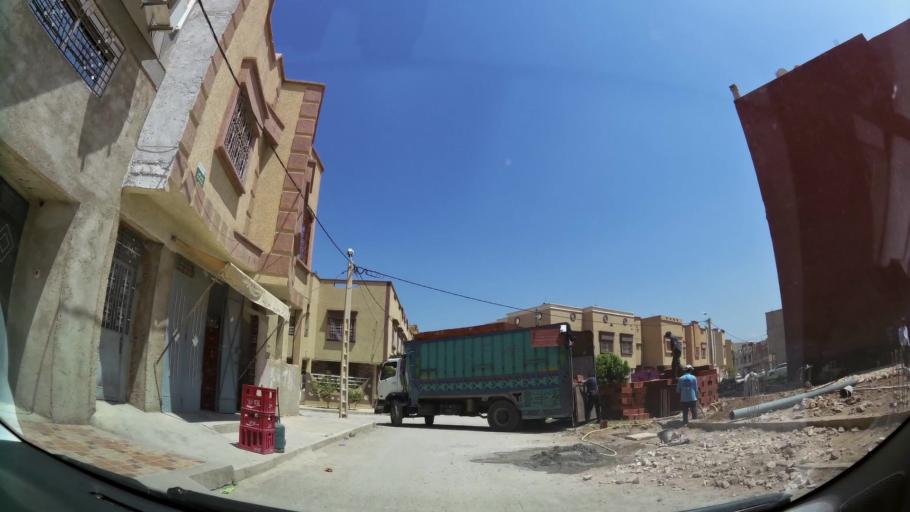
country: MA
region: Oriental
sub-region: Oujda-Angad
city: Oujda
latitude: 34.6952
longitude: -1.8894
